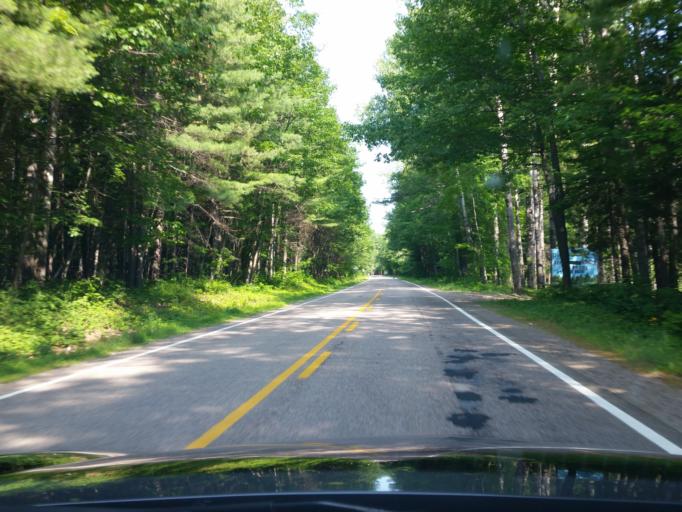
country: CA
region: Quebec
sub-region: Outaouais
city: Shawville
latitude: 45.5219
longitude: -76.4331
